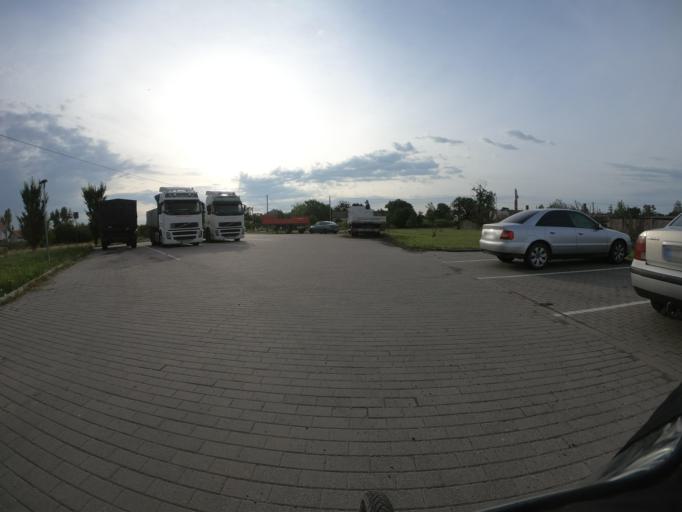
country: HU
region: Hajdu-Bihar
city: Hortobagy
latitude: 47.6055
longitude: 21.0717
